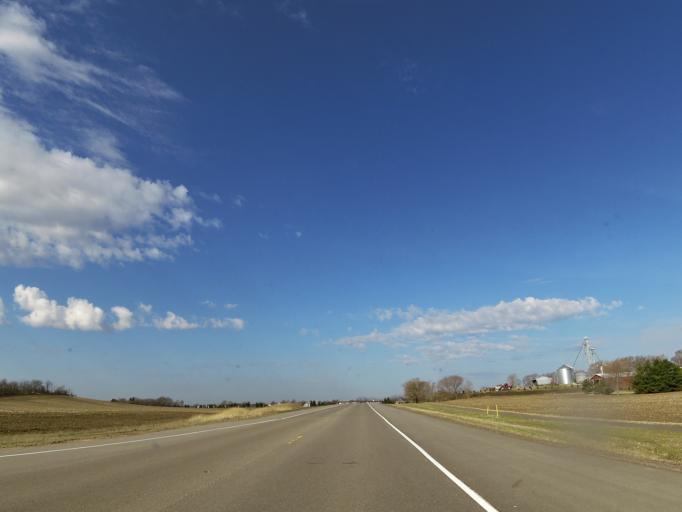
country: US
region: Minnesota
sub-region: Washington County
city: Cottage Grove
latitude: 44.8477
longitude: -92.8941
